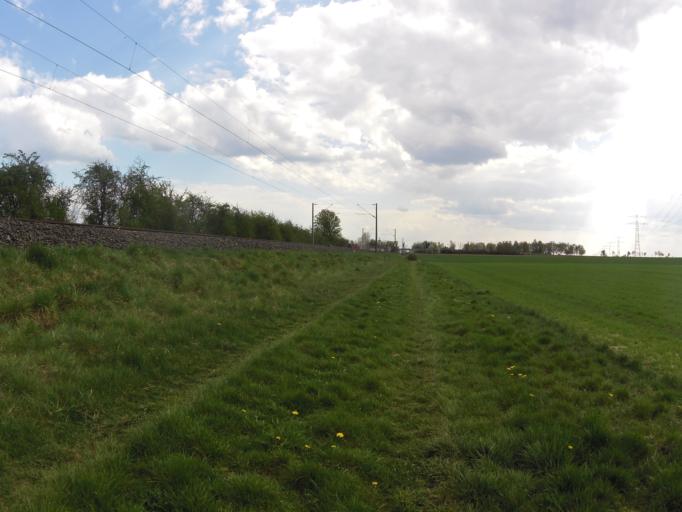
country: DE
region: Bavaria
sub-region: Regierungsbezirk Unterfranken
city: Oberpleichfeld
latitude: 49.8613
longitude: 10.1009
